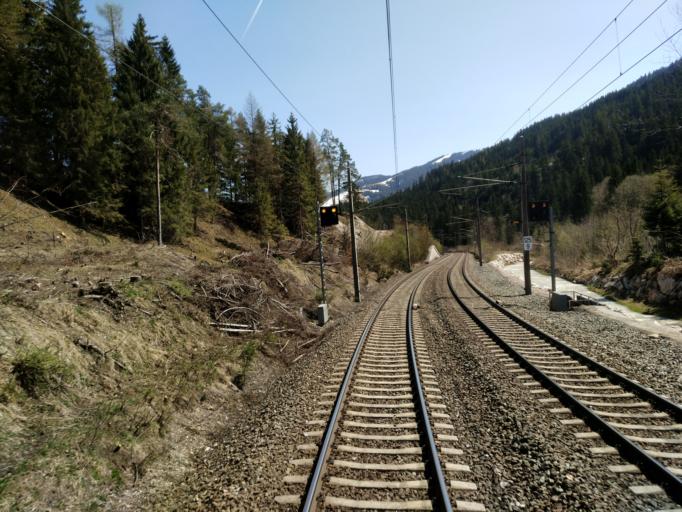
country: AT
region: Tyrol
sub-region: Politischer Bezirk Kitzbuhel
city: Hochfilzen
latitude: 47.4525
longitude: 12.6748
